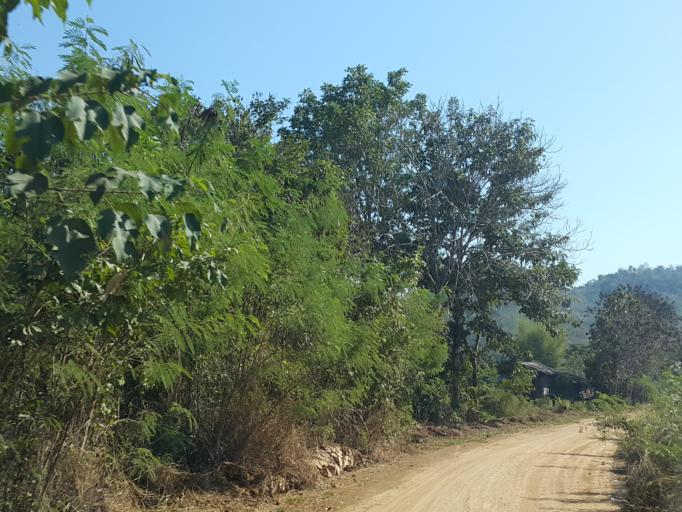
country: TH
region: Sukhothai
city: Thung Saliam
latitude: 17.3154
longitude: 99.4434
